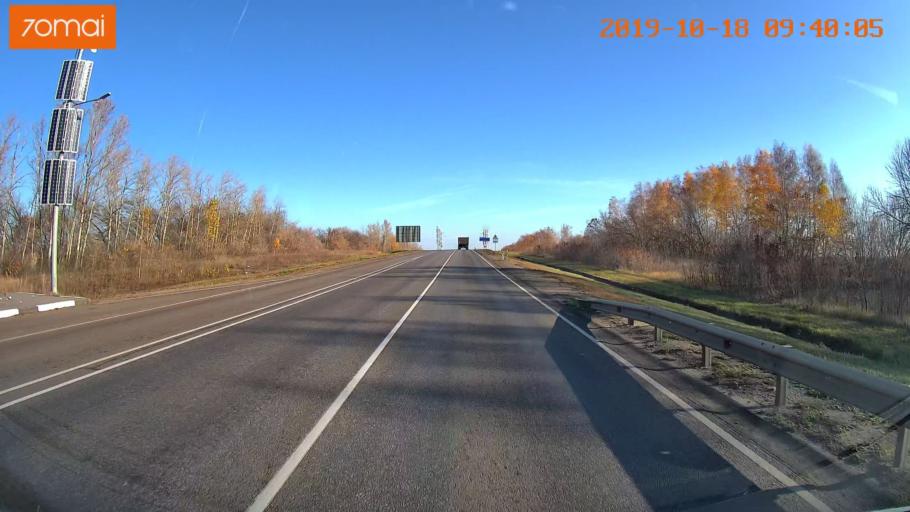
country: RU
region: Tula
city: Yefremov
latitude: 53.2600
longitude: 38.1432
